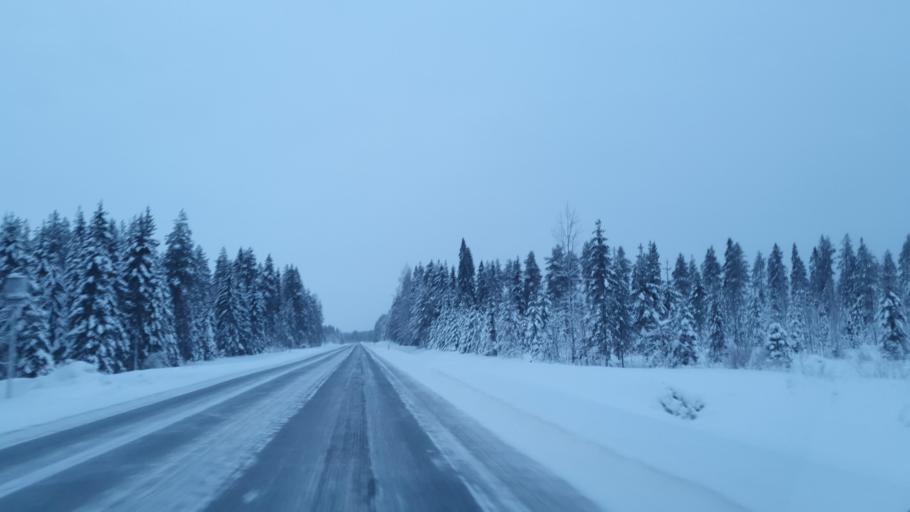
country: FI
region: Kainuu
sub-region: Kajaani
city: Vaala
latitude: 64.6167
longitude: 26.6083
